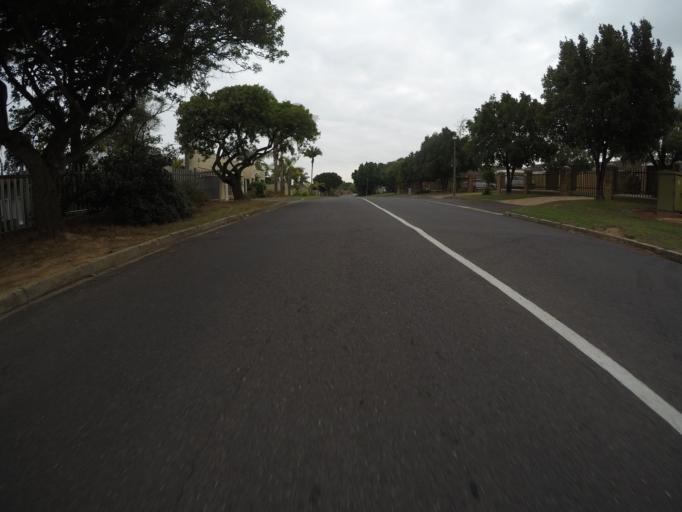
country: ZA
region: Western Cape
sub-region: City of Cape Town
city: Kraaifontein
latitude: -33.8684
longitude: 18.6492
